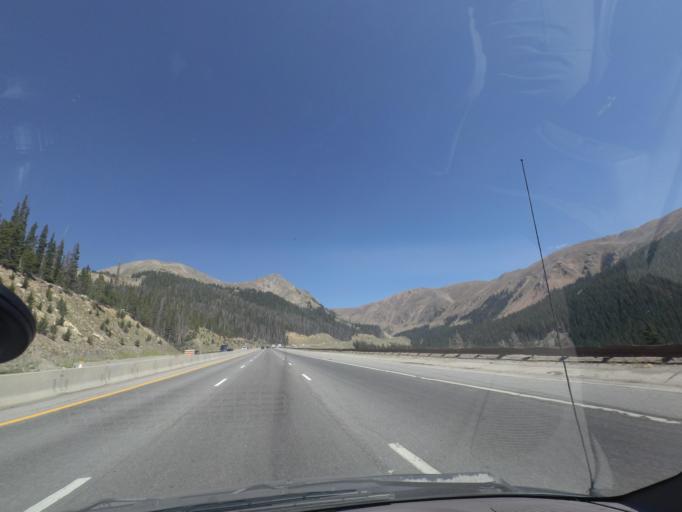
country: US
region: Colorado
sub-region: Summit County
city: Keystone
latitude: 39.6746
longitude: -105.9590
